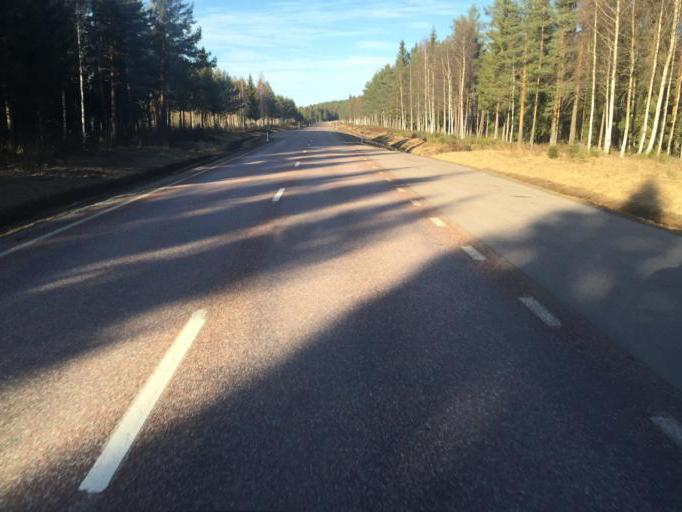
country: SE
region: Dalarna
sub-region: Vansbro Kommun
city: Jarna
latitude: 60.4667
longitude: 14.6008
